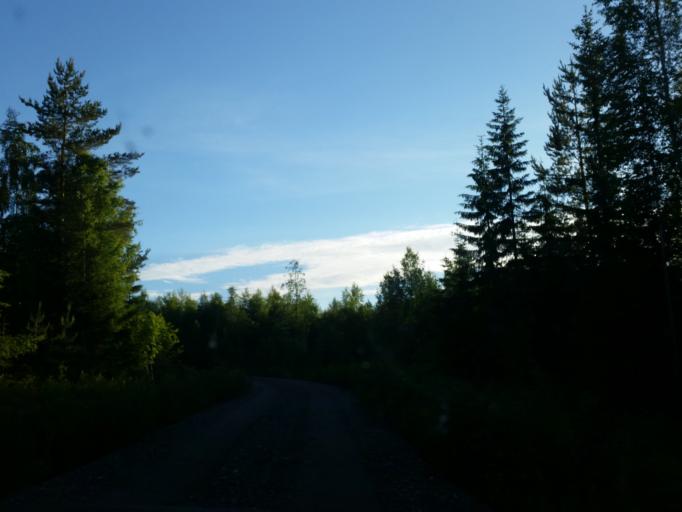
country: FI
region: Northern Savo
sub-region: Sisae-Savo
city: Tervo
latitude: 63.0532
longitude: 26.6579
